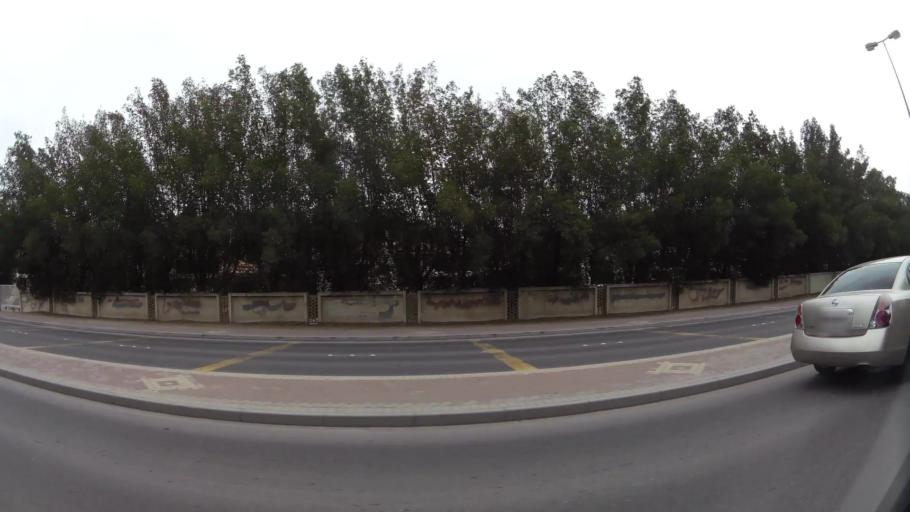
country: BH
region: Manama
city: Jidd Hafs
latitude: 26.2065
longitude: 50.5339
